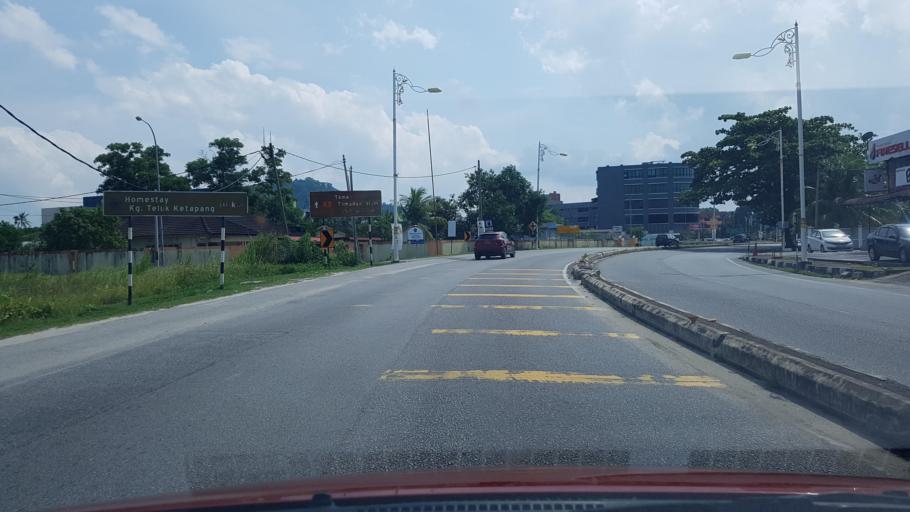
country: MY
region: Terengganu
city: Kuala Terengganu
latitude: 5.3142
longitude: 103.1471
